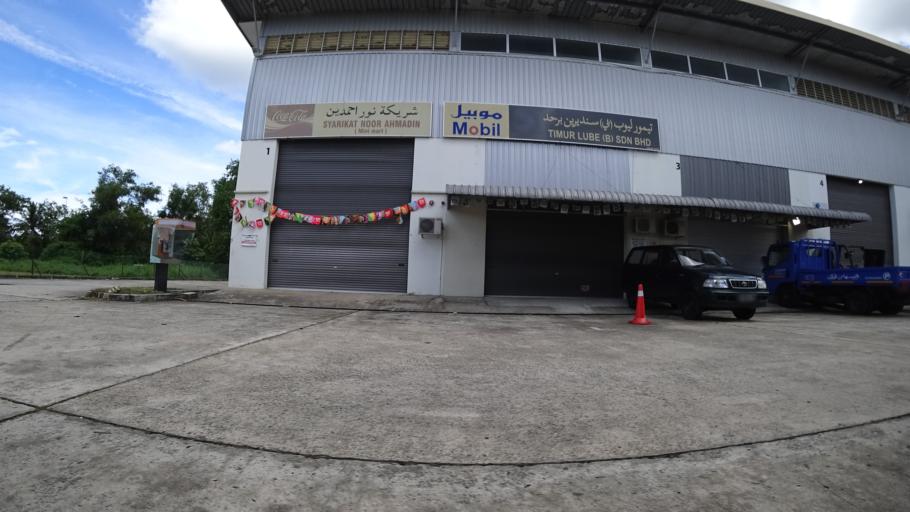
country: MY
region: Sarawak
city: Limbang
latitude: 4.8128
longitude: 114.8580
